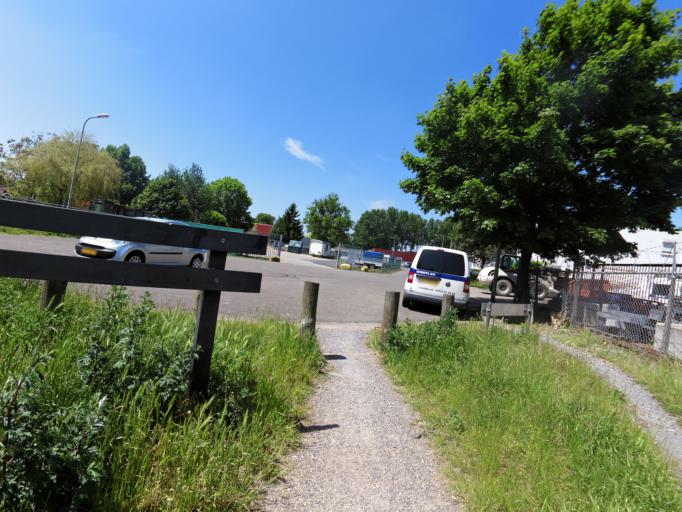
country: NL
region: Limburg
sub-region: Gemeente Kerkrade
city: Kerkrade
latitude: 50.9121
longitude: 6.0340
